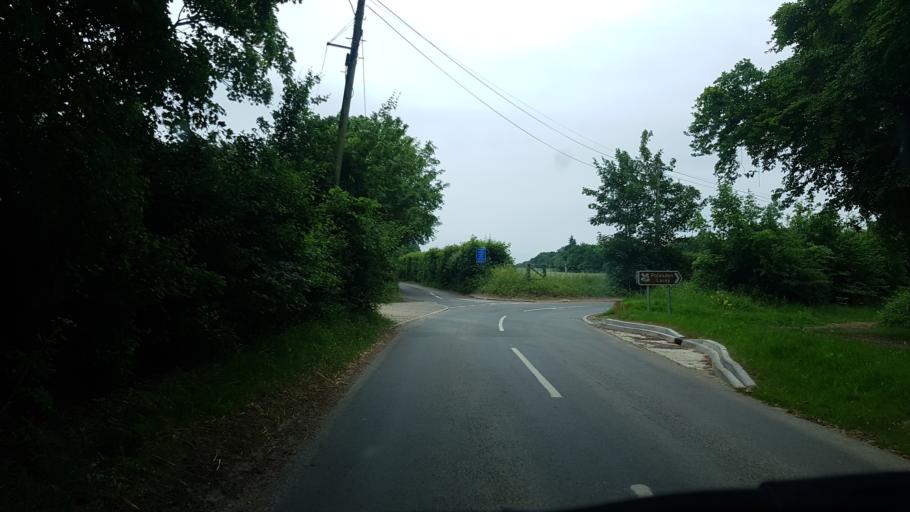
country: GB
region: England
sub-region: Surrey
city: Great Bookham
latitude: 51.2678
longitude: -0.3664
